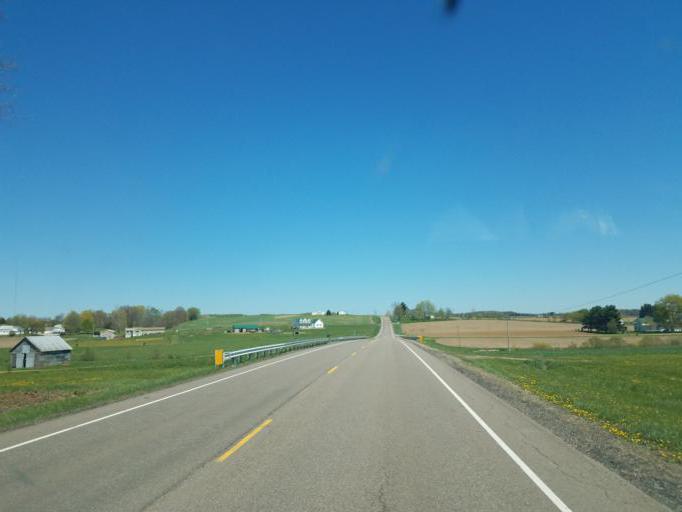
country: US
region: Ohio
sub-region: Knox County
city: Fredericktown
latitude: 40.5284
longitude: -82.5462
